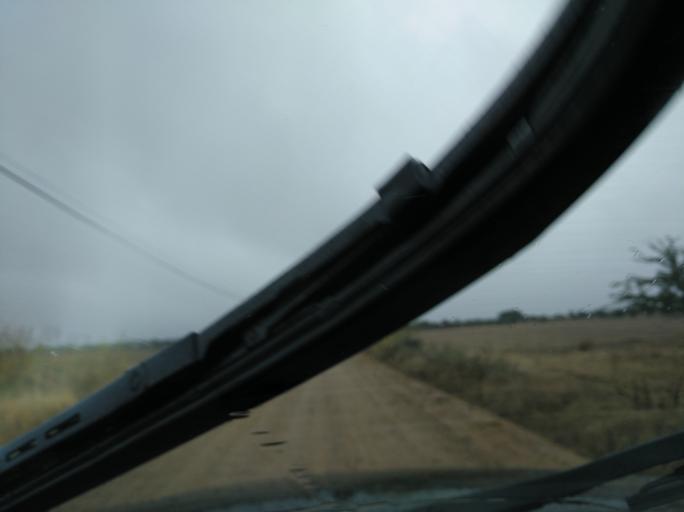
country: PT
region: Portalegre
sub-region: Campo Maior
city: Campo Maior
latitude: 38.9617
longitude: -7.0720
